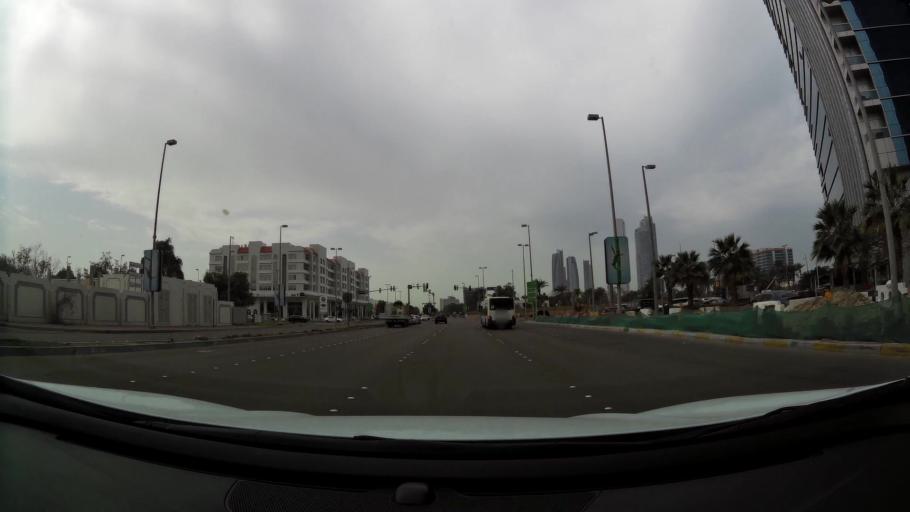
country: AE
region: Abu Dhabi
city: Abu Dhabi
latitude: 24.4676
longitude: 54.3404
